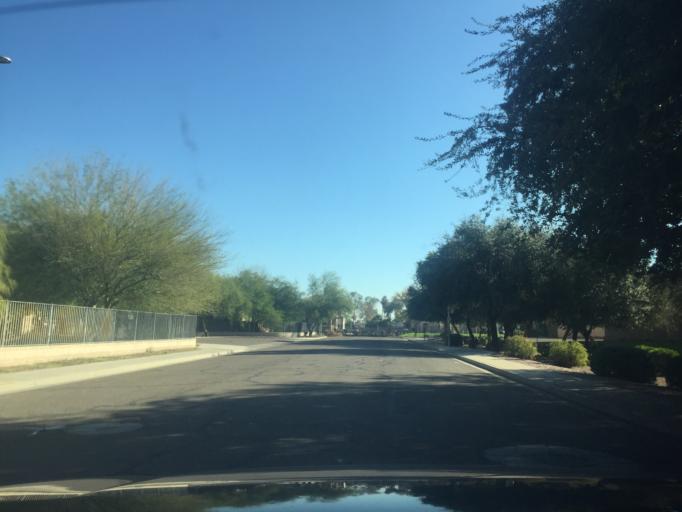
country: US
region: Arizona
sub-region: Maricopa County
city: Tolleson
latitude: 33.4765
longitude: -112.2185
